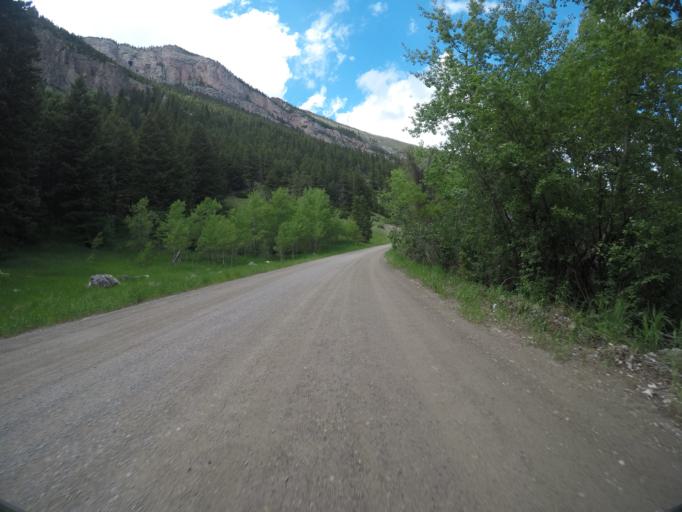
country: US
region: Montana
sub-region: Park County
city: Livingston
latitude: 45.5393
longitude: -110.2149
